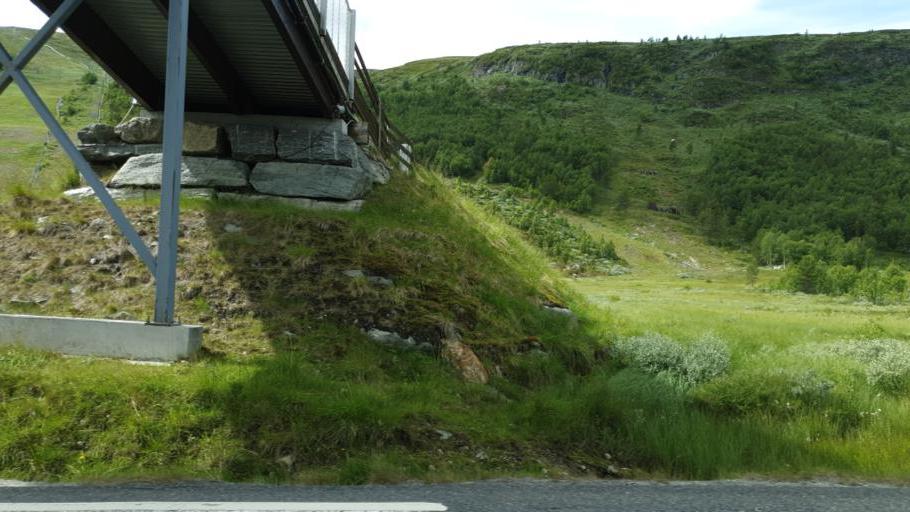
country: NO
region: Oppland
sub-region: Vaga
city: Vagamo
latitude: 61.7558
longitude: 9.0710
